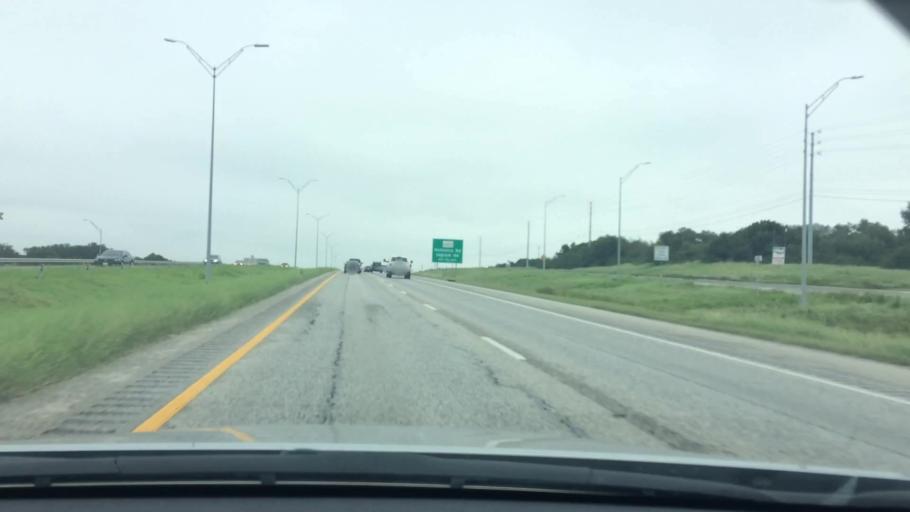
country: US
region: Texas
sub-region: Bexar County
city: Leon Valley
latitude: 29.4597
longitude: -98.6901
